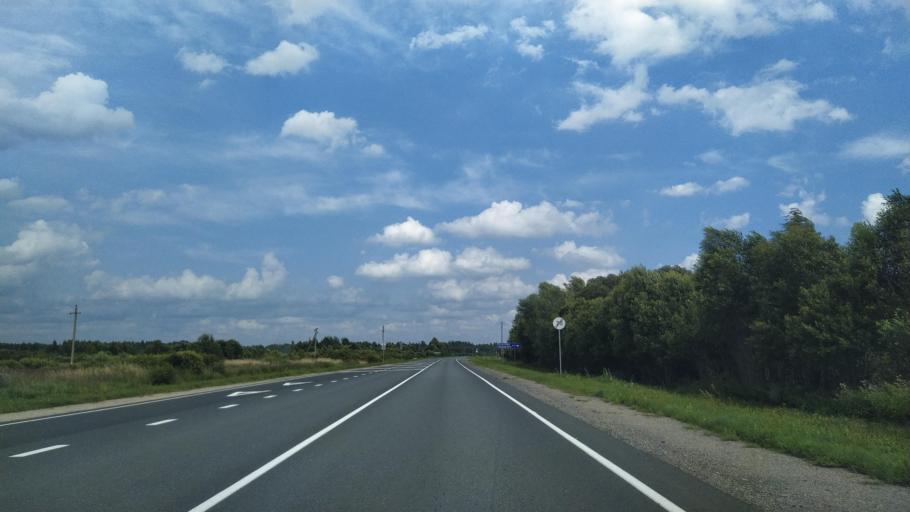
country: RU
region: Pskov
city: Dno
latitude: 57.9824
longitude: 29.7516
